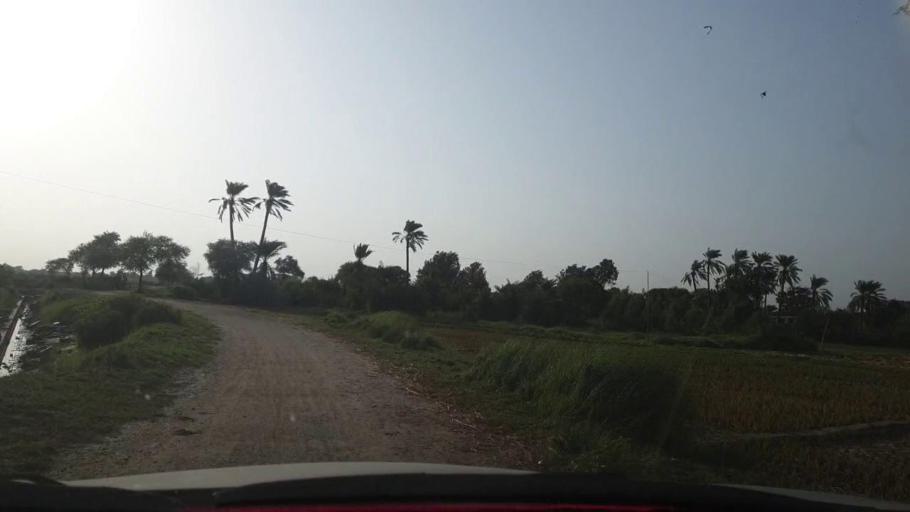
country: PK
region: Sindh
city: Talhar
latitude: 24.9092
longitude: 68.8164
